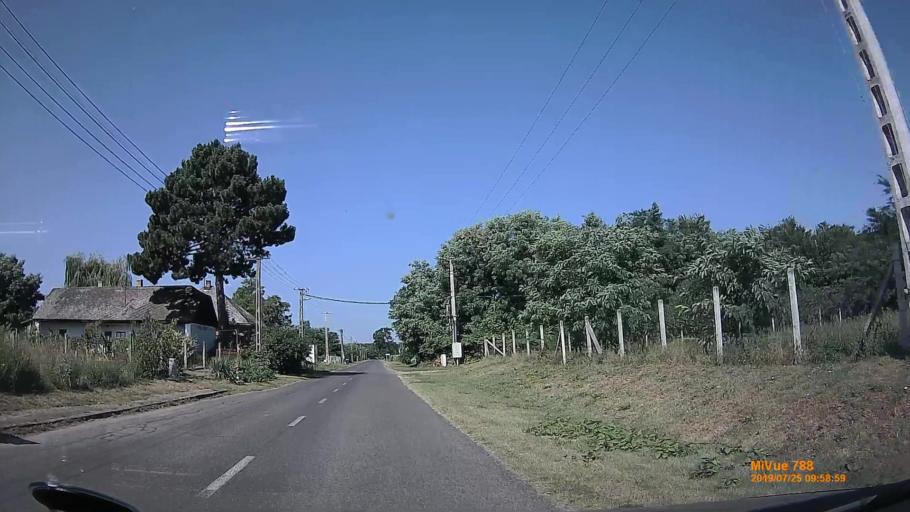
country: HU
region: Szabolcs-Szatmar-Bereg
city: Nyirpazony
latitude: 48.0289
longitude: 21.7739
